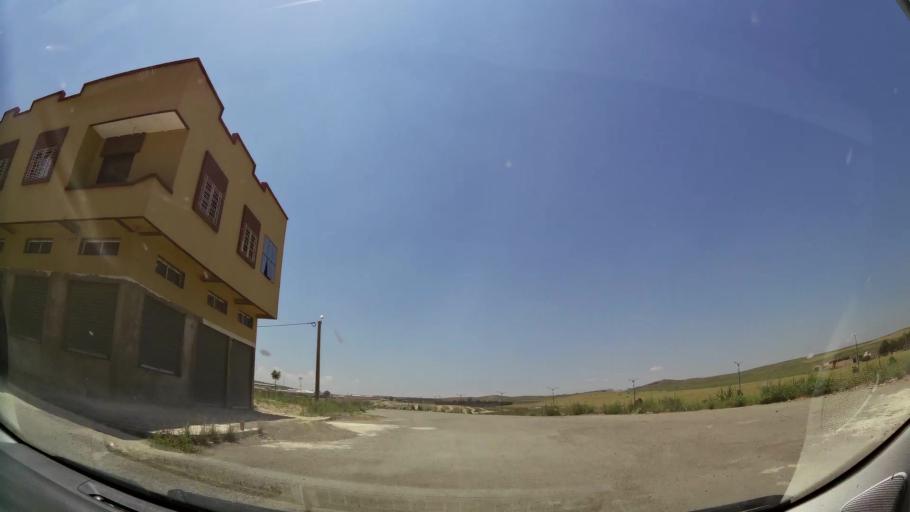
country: MA
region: Oriental
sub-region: Oujda-Angad
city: Oujda
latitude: 34.6596
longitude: -1.9541
